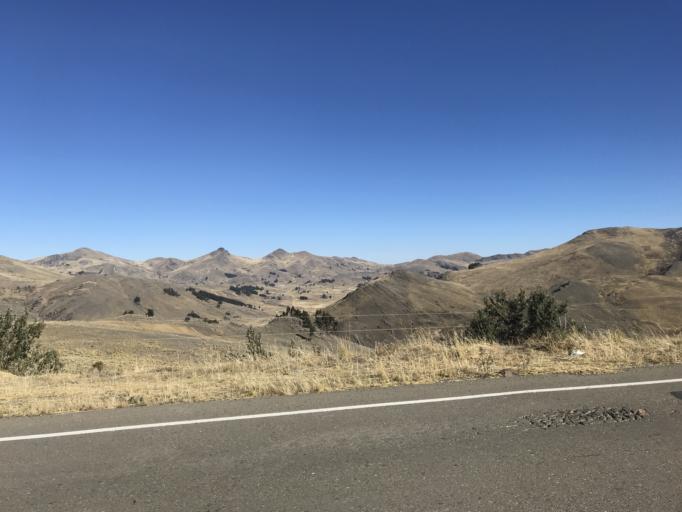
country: PE
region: Puno
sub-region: Yunguyo
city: Yunguyo
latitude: -16.1836
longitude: -68.9818
